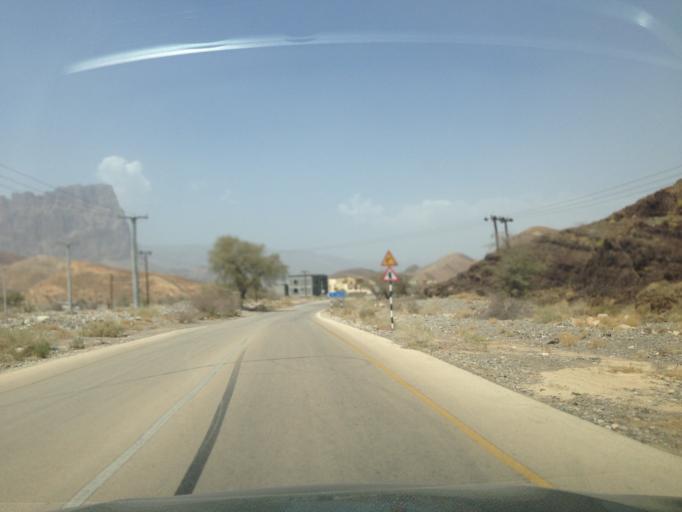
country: OM
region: Muhafazat ad Dakhiliyah
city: Bahla'
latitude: 23.2026
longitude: 56.9444
